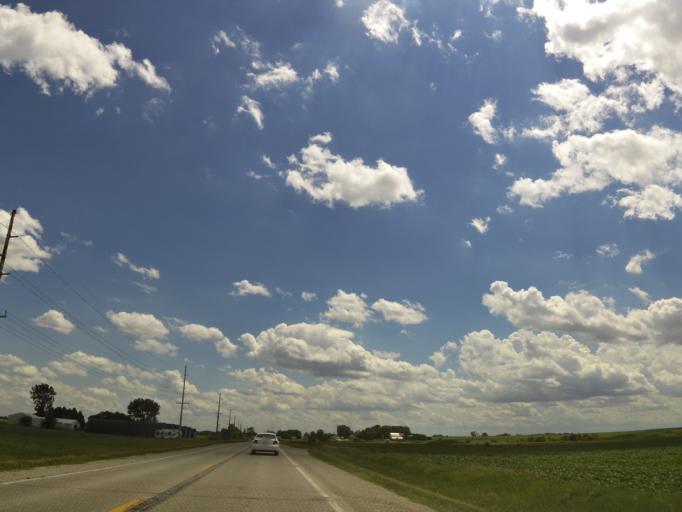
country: US
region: Iowa
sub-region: Buchanan County
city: Independence
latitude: 42.4162
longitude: -91.8899
